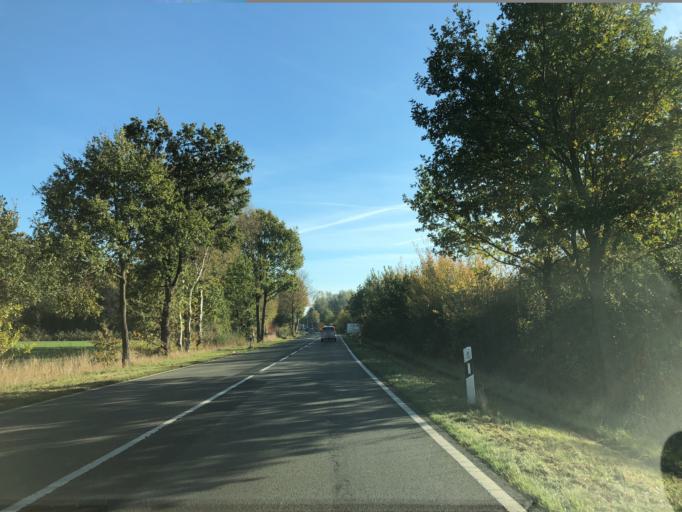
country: DE
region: Lower Saxony
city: Lehe
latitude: 53.0501
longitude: 7.3237
